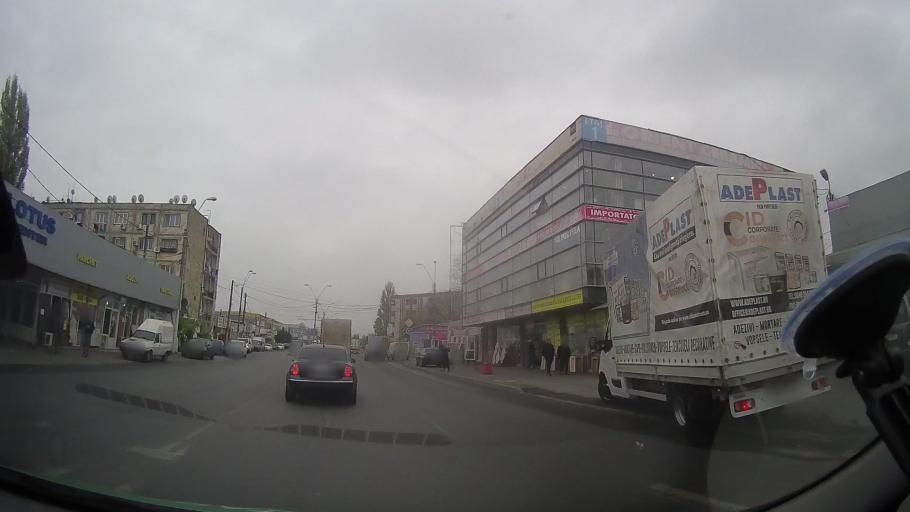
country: RO
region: Ilfov
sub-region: Comuna Chiajna
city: Rosu
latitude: 44.4294
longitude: 26.0026
